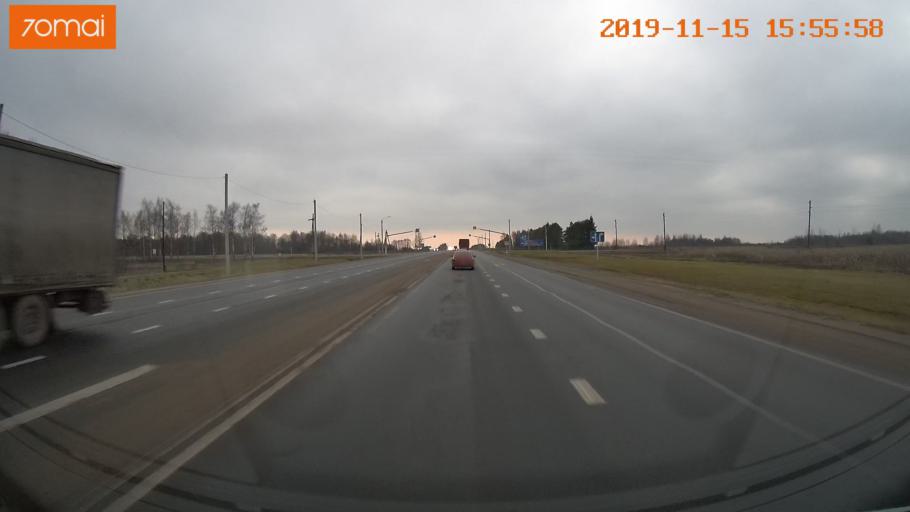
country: RU
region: Jaroslavl
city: Yaroslavl
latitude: 57.8471
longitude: 39.9782
